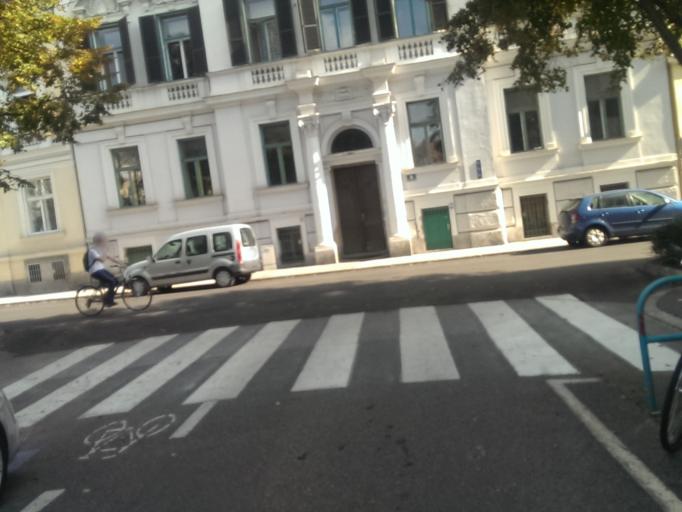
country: AT
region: Styria
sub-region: Graz Stadt
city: Graz
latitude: 47.0678
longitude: 15.4537
